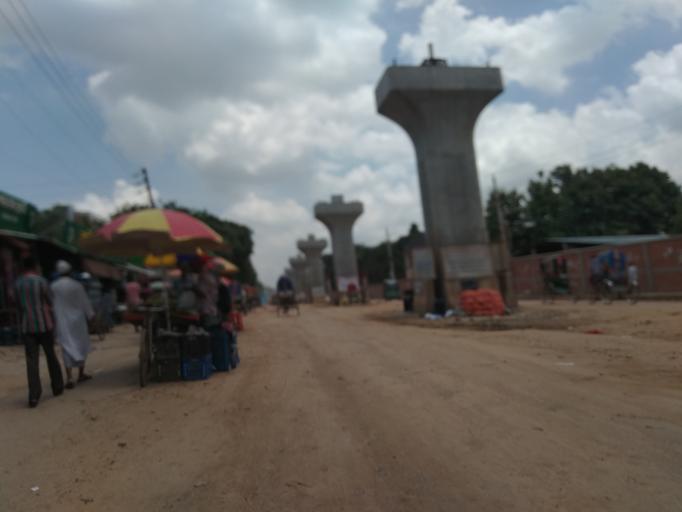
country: BD
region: Dhaka
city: Tungi
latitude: 23.8300
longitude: 90.3637
